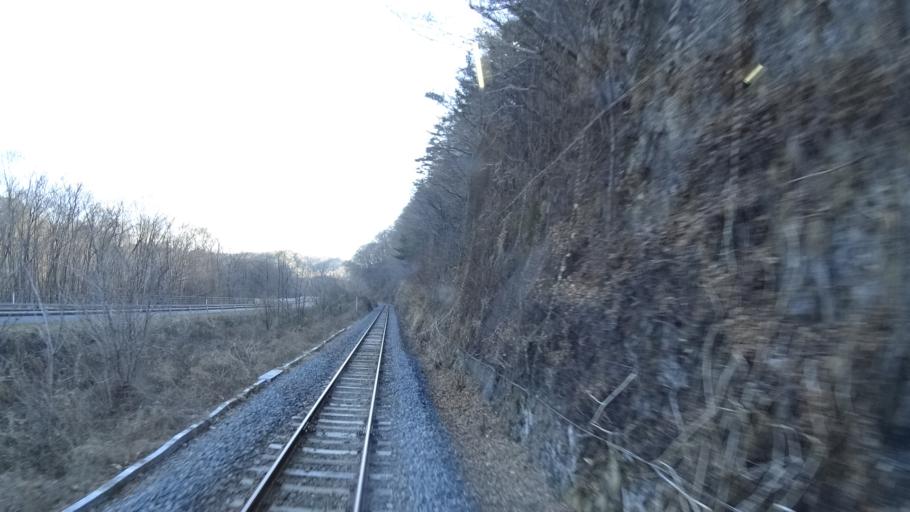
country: JP
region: Iwate
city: Yamada
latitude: 39.5548
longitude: 141.9400
